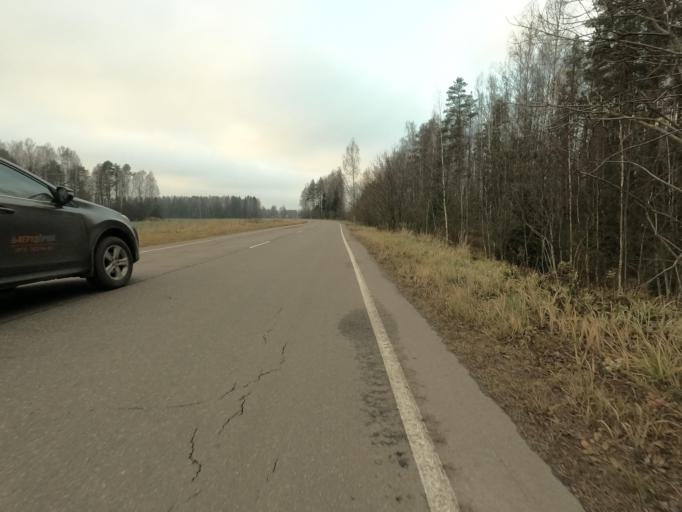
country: RU
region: Leningrad
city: Kirovsk
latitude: 59.8002
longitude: 30.9986
